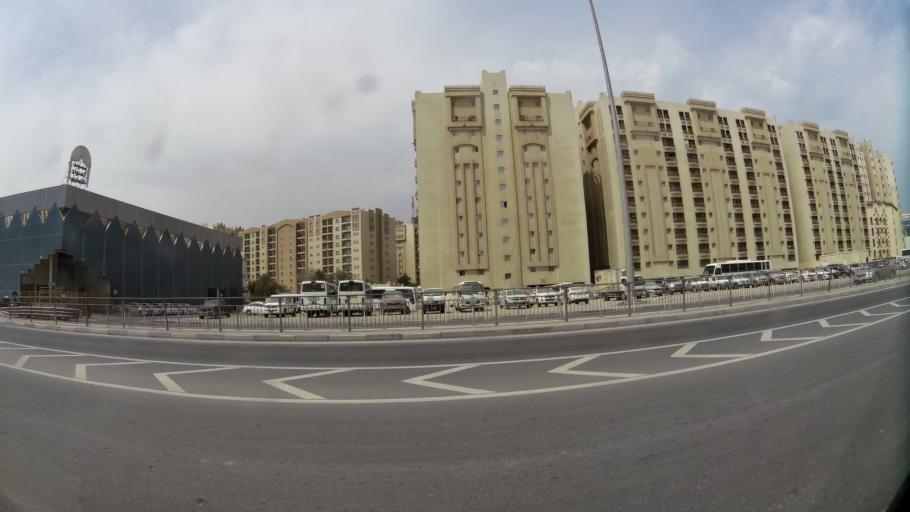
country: QA
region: Baladiyat ad Dawhah
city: Doha
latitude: 25.2799
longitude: 51.5214
